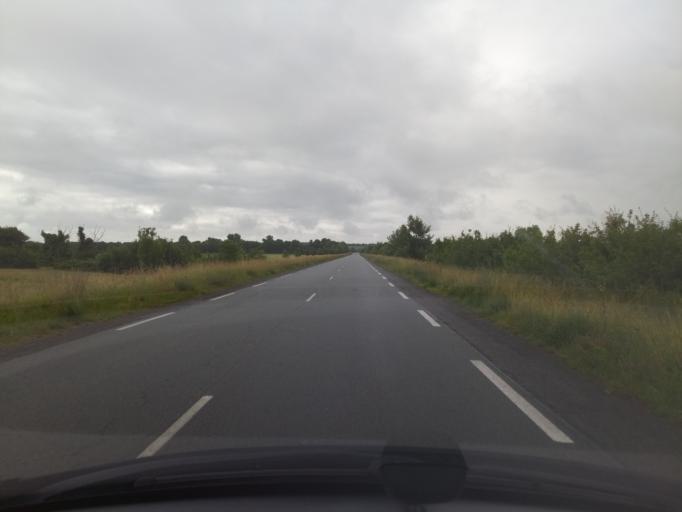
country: FR
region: Poitou-Charentes
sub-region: Departement de la Charente-Maritime
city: Courcon
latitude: 46.1935
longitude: -0.8627
